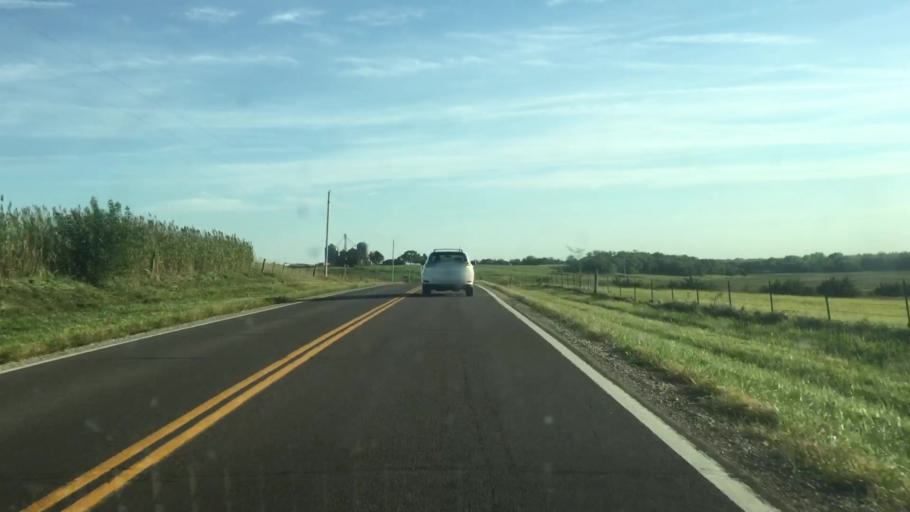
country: US
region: Kansas
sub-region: Brown County
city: Horton
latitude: 39.5824
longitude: -95.5270
